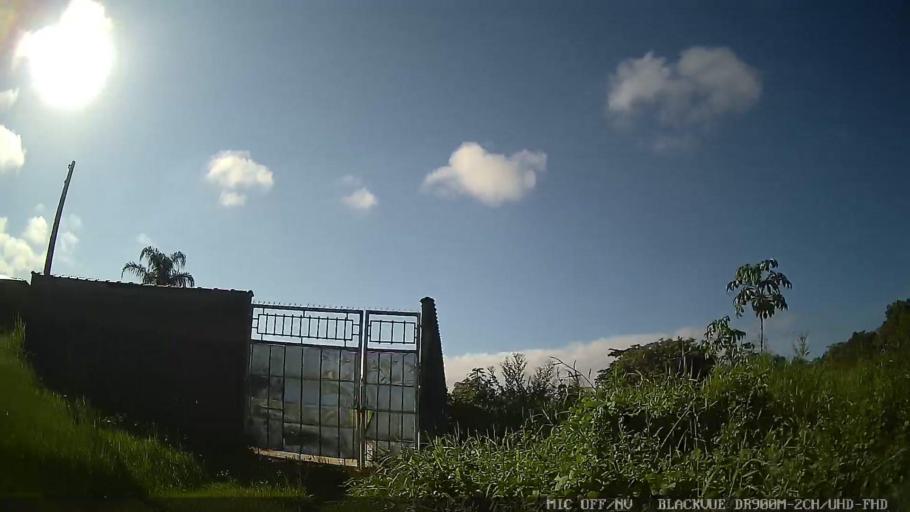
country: BR
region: Sao Paulo
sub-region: Peruibe
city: Peruibe
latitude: -24.2670
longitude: -46.9410
